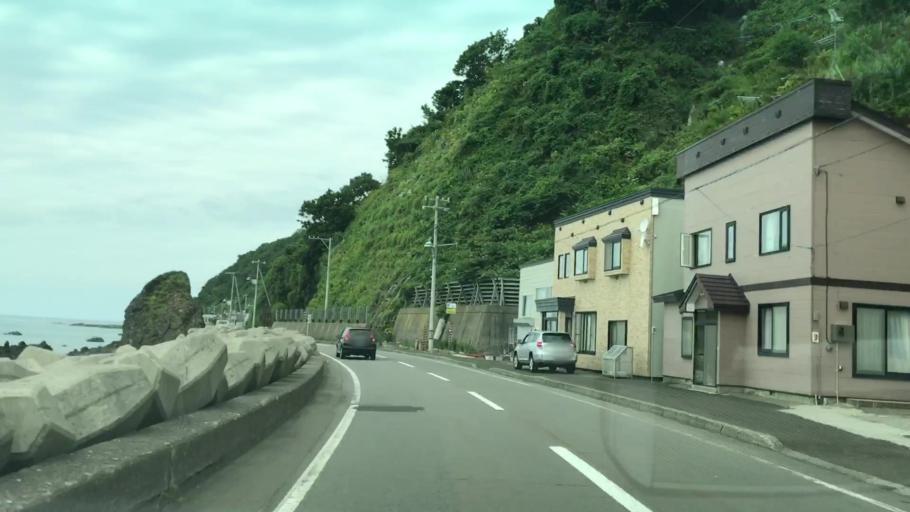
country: JP
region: Hokkaido
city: Iwanai
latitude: 43.1592
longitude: 140.4004
